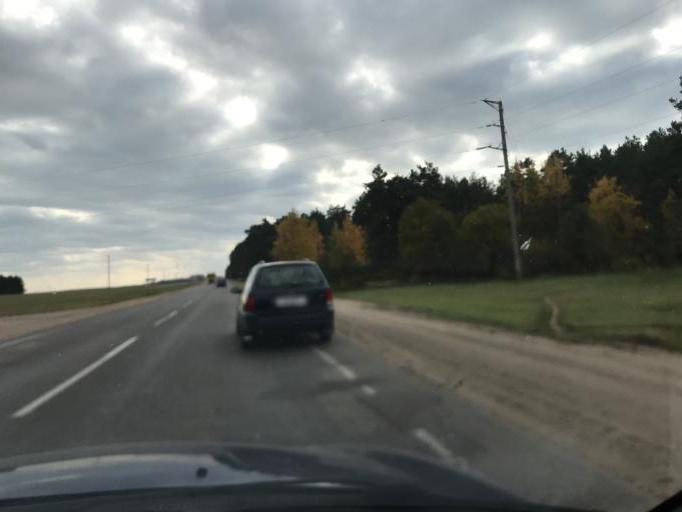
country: BY
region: Grodnenskaya
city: Lida
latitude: 53.8880
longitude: 25.2535
